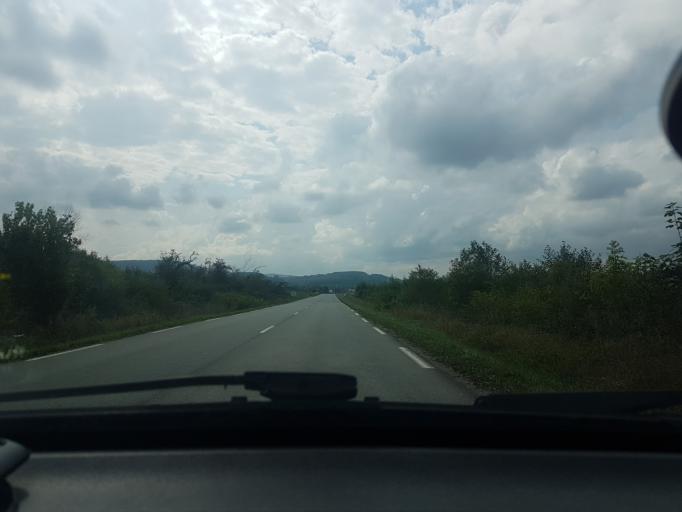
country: FR
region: Franche-Comte
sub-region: Departement du Doubs
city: Arcey
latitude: 47.5588
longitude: 6.6027
